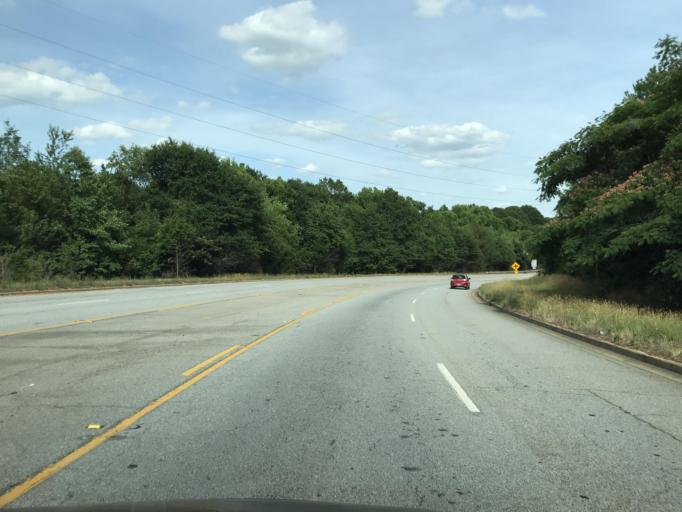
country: US
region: South Carolina
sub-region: Greenville County
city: Gantt
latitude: 34.7954
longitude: -82.4166
